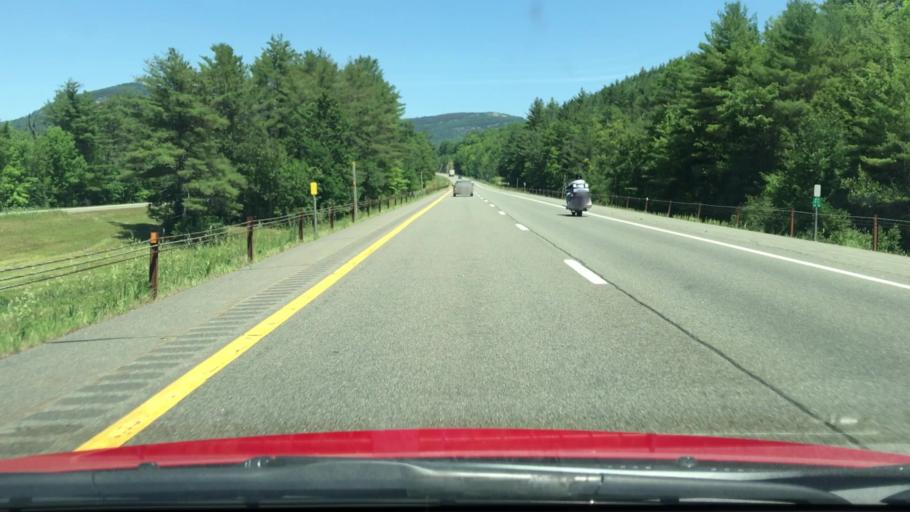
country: US
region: New York
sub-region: Essex County
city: Elizabethtown
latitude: 44.3568
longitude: -73.5318
